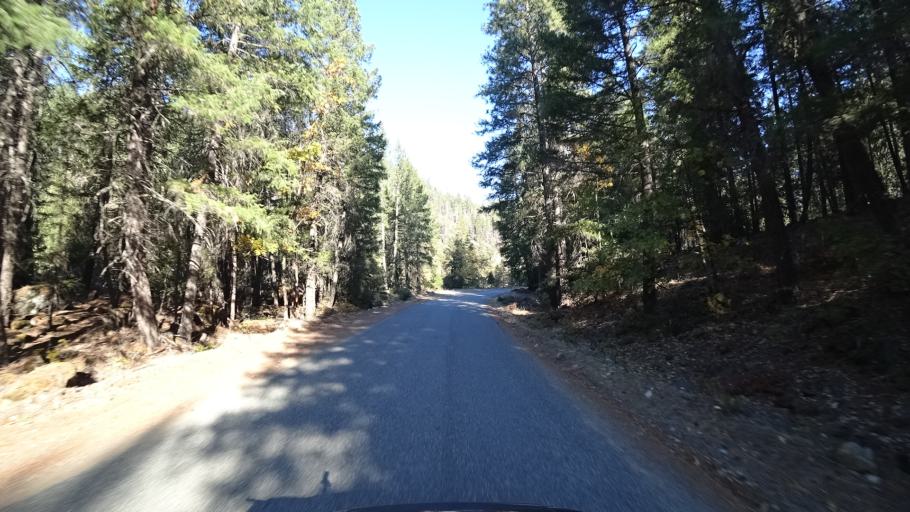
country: US
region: California
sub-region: Siskiyou County
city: Happy Camp
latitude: 41.6465
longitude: -123.1142
